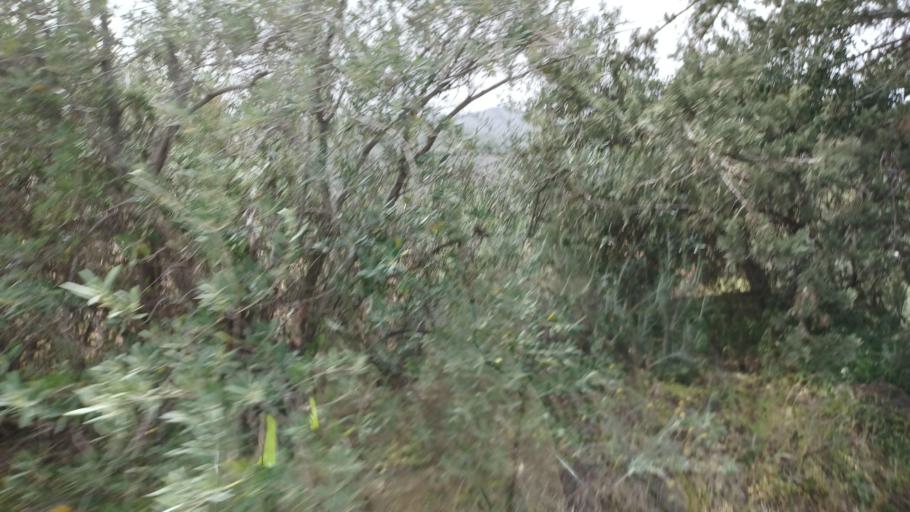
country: CY
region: Limassol
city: Parekklisha
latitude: 34.8481
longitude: 33.1021
